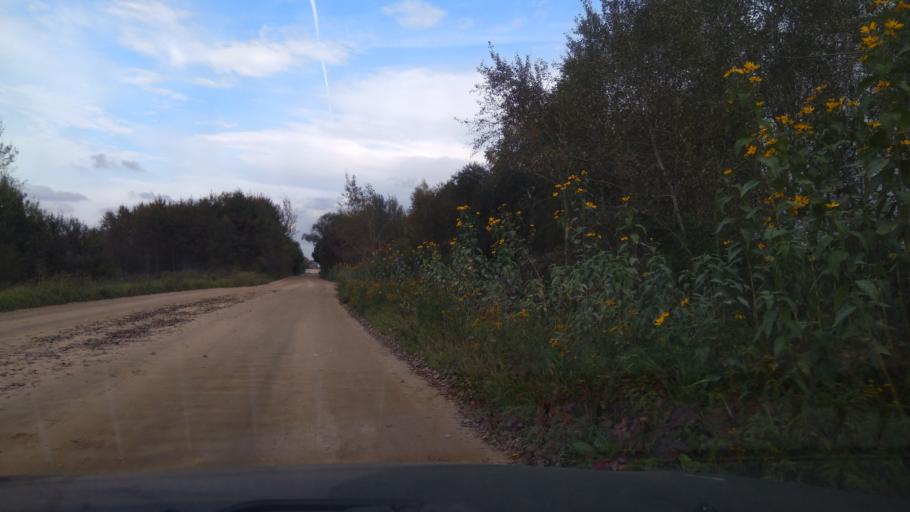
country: BY
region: Minsk
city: Rudzyensk
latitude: 53.6149
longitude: 27.8468
